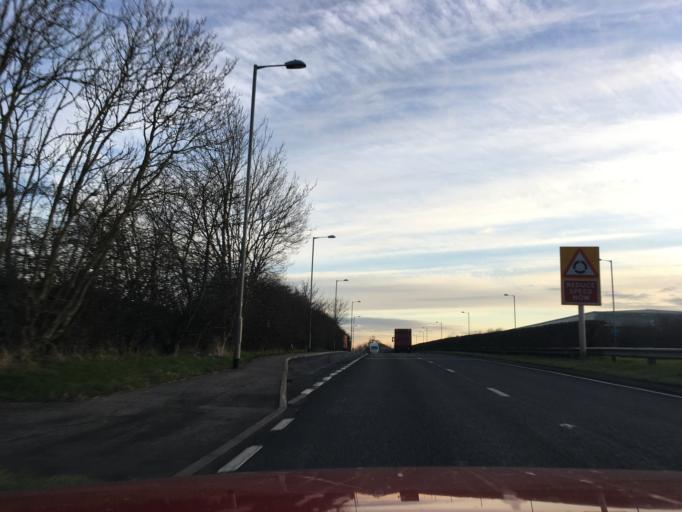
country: GB
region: England
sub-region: Staffordshire
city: Stafford
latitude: 52.8366
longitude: -2.1343
